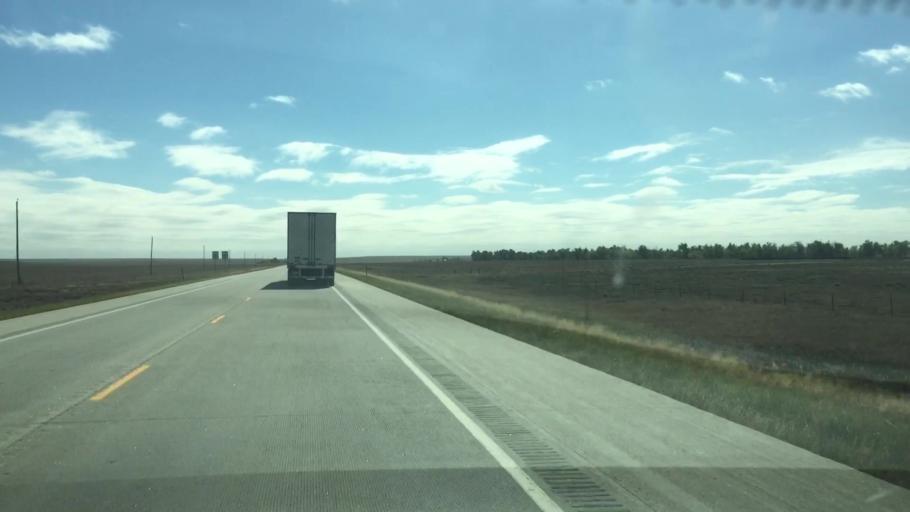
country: US
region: Colorado
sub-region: Lincoln County
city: Hugo
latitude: 39.0660
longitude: -103.3690
